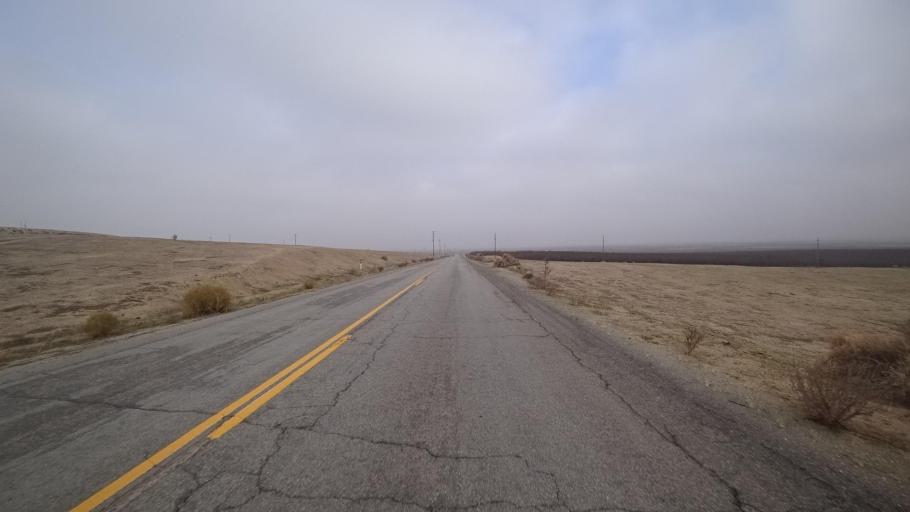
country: US
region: California
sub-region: Kern County
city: Maricopa
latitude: 35.1343
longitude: -119.3525
